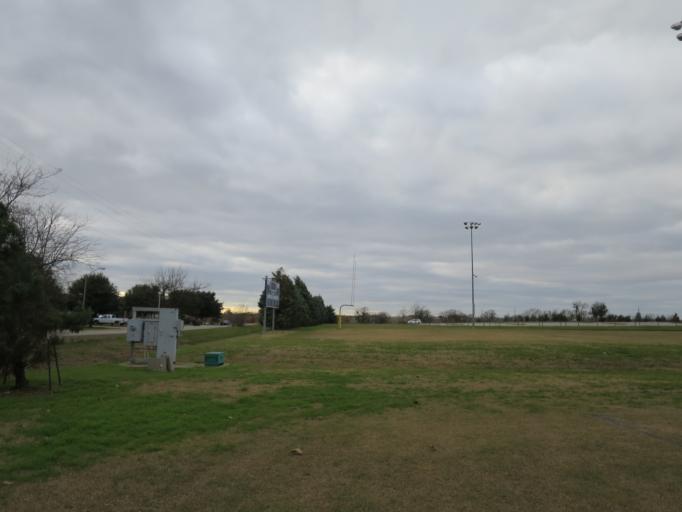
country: US
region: Texas
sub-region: Williamson County
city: Round Rock
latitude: 30.5403
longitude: -97.6233
